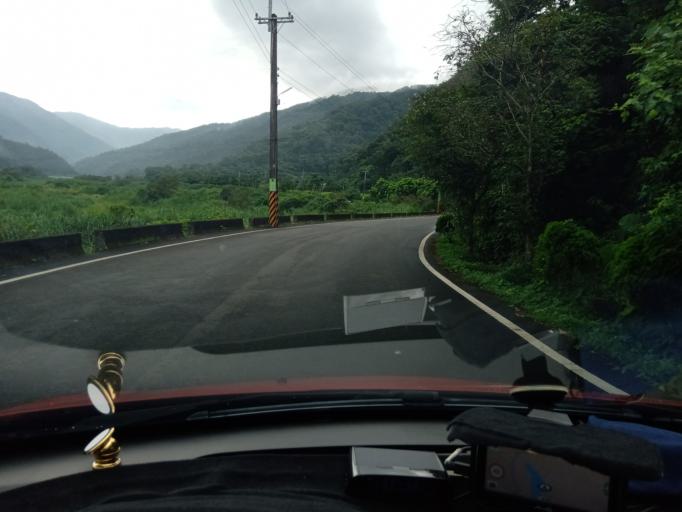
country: TW
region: Taiwan
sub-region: Yilan
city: Yilan
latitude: 24.7823
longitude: 121.7047
